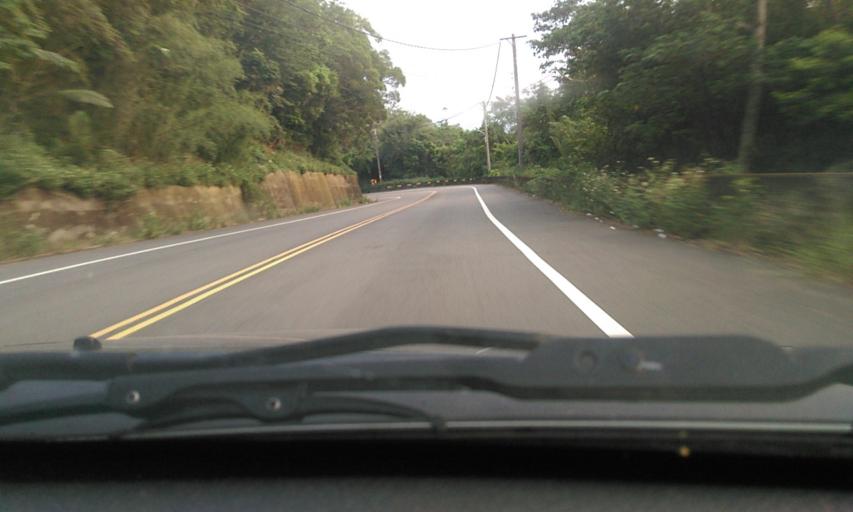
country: TW
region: Taiwan
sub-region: Hsinchu
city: Hsinchu
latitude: 24.6855
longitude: 120.9793
